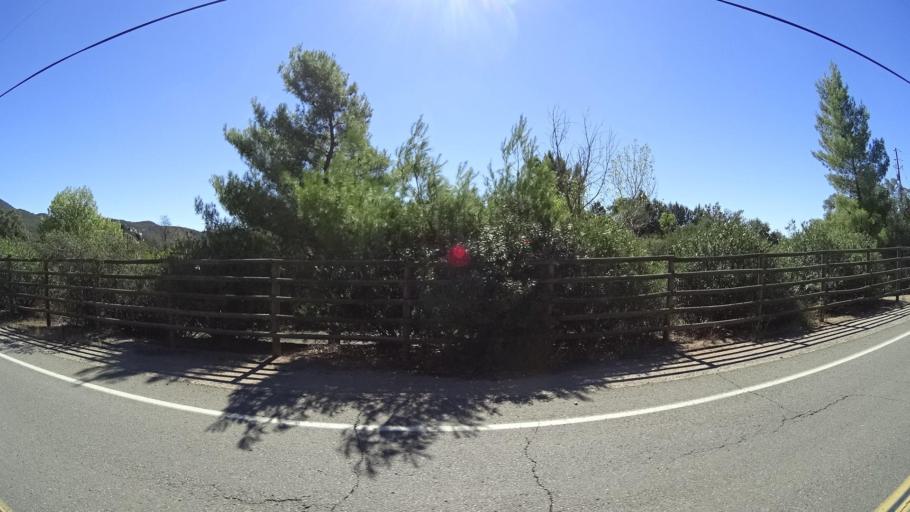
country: US
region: California
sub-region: San Diego County
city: Descanso
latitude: 32.8029
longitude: -116.6425
